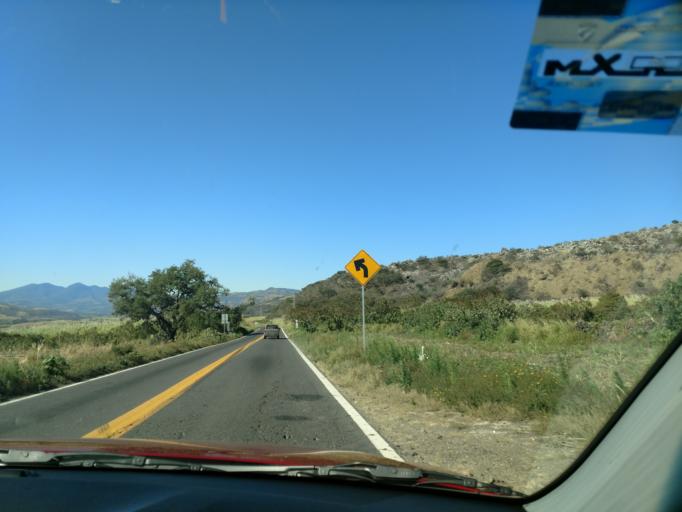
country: MX
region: Nayarit
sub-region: Ahuacatlan
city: Ahuacatlan
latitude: 21.1083
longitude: -104.5872
